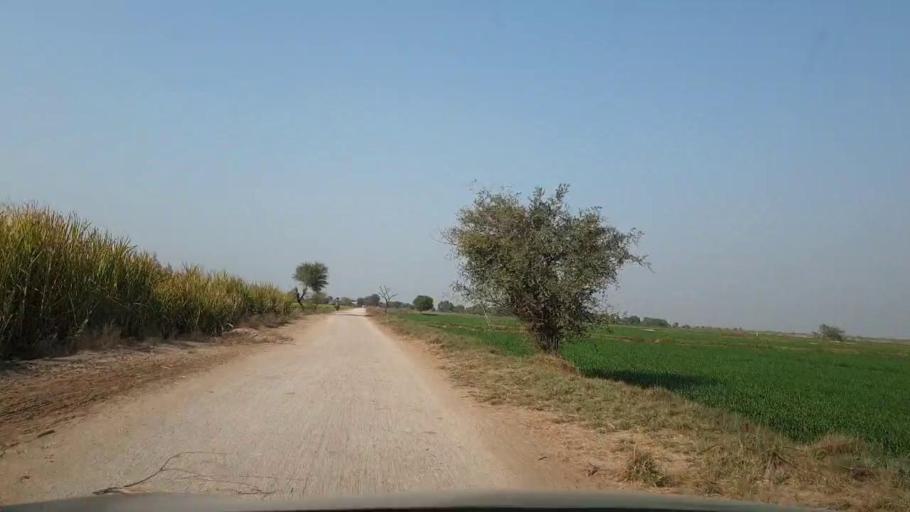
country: PK
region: Sindh
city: Tando Allahyar
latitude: 25.5780
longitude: 68.7942
